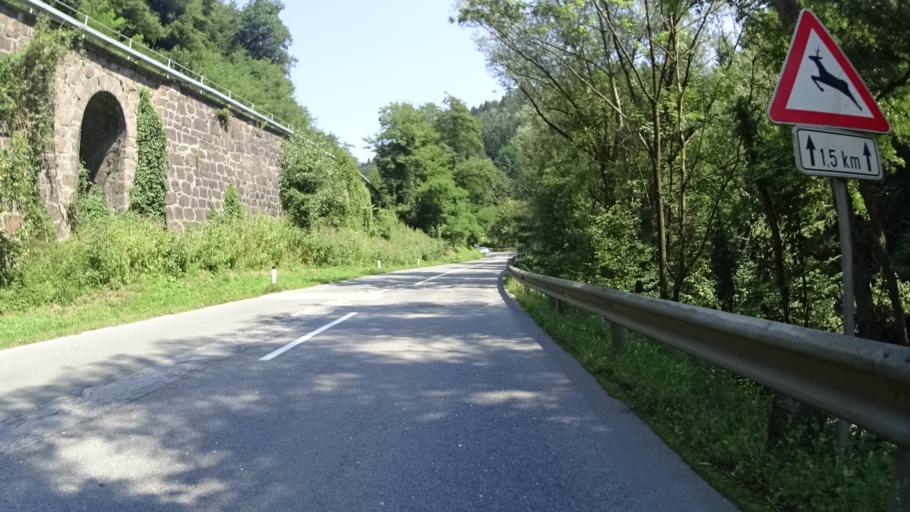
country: SI
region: Ravne na Koroskem
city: Ravne na Koroskem
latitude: 46.5477
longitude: 14.9722
